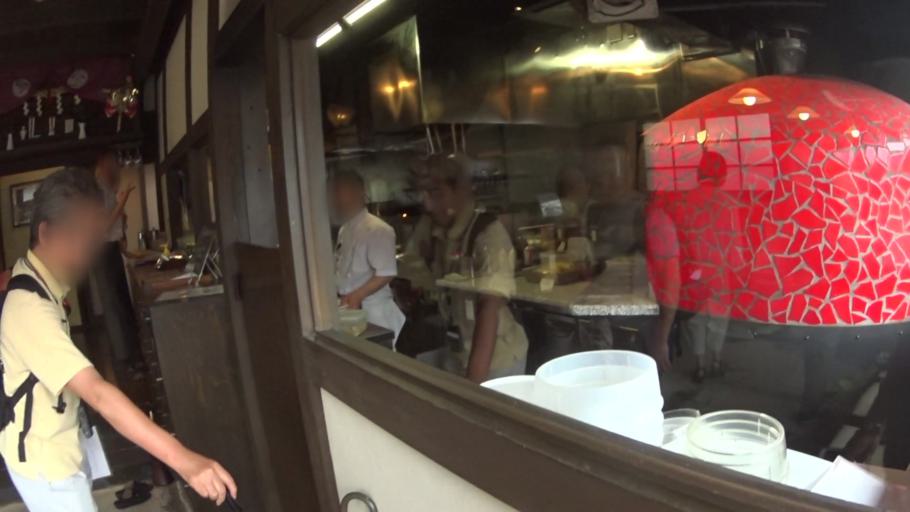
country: JP
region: Chiba
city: Nagareyama
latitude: 35.8572
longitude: 139.8994
